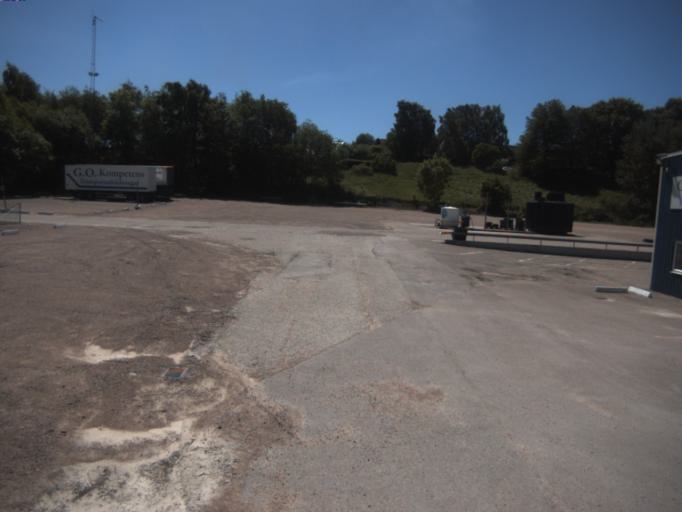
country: SE
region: Skane
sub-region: Helsingborg
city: Glumslov
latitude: 55.9646
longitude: 12.8561
